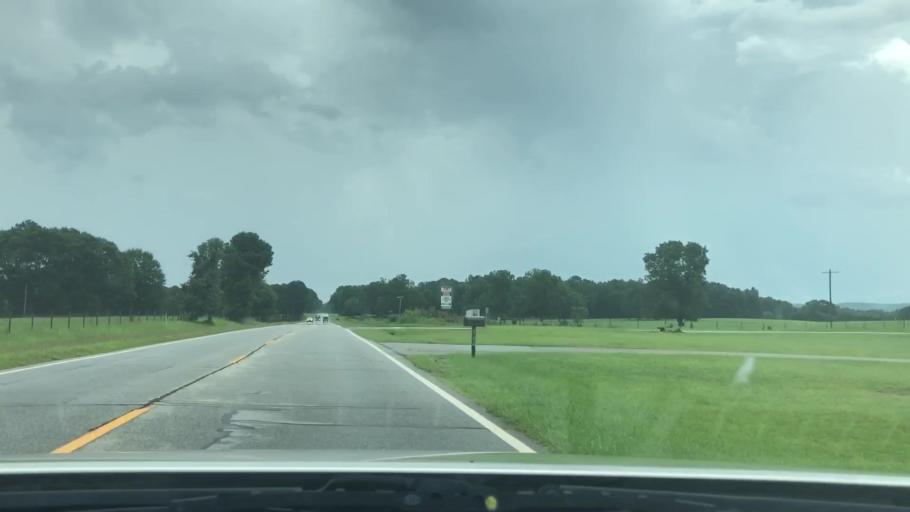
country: US
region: Georgia
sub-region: Pike County
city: Zebulon
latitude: 33.0947
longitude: -84.2831
